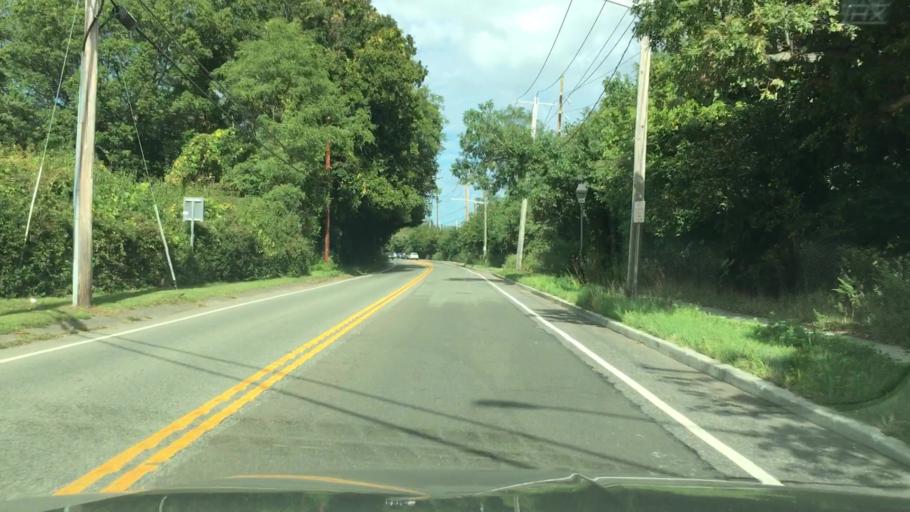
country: US
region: New York
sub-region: Suffolk County
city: Stony Brook
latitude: 40.9175
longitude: -73.1310
